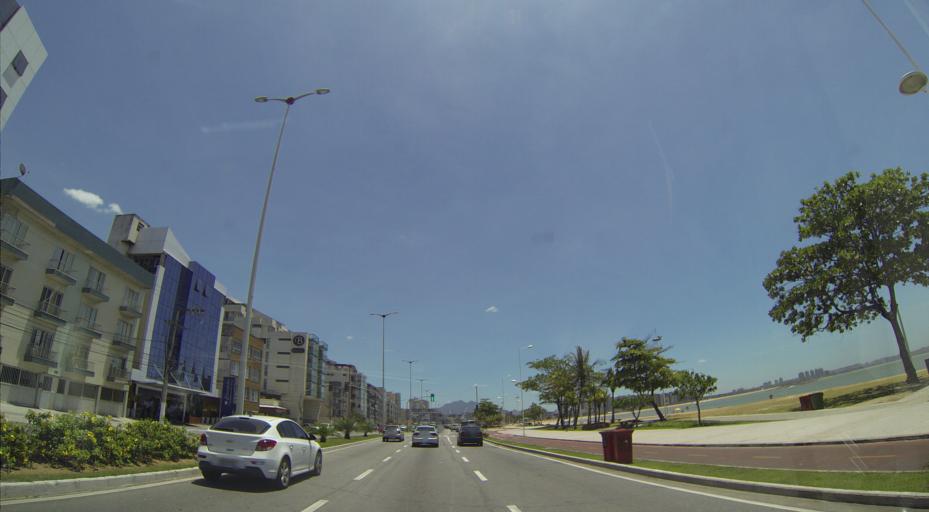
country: BR
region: Espirito Santo
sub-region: Vila Velha
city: Vila Velha
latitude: -20.2914
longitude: -40.2901
